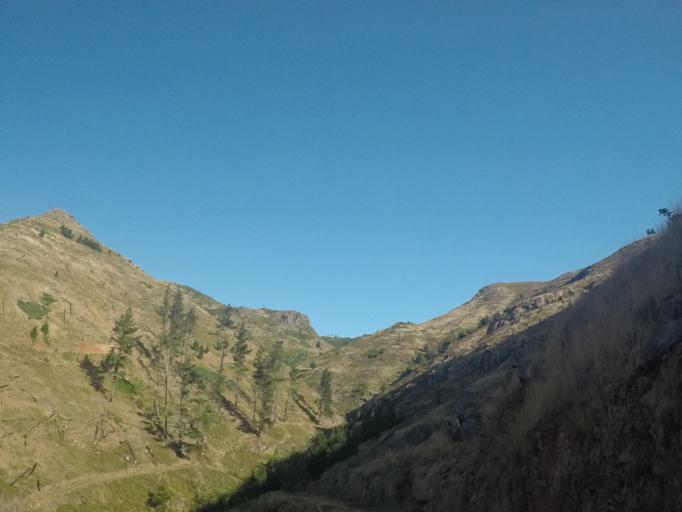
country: PT
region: Madeira
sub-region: Funchal
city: Nossa Senhora do Monte
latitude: 32.7086
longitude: -16.9010
